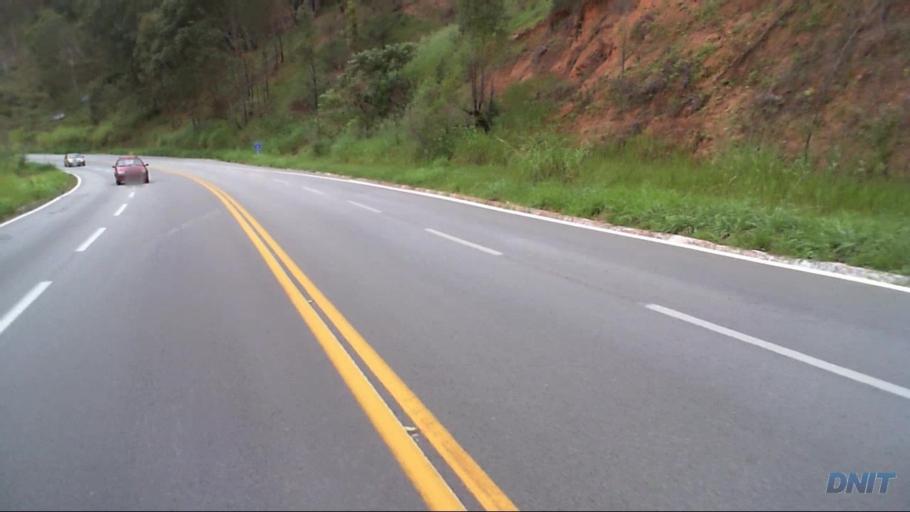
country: BR
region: Minas Gerais
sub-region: Joao Monlevade
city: Joao Monlevade
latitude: -19.8440
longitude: -43.1029
